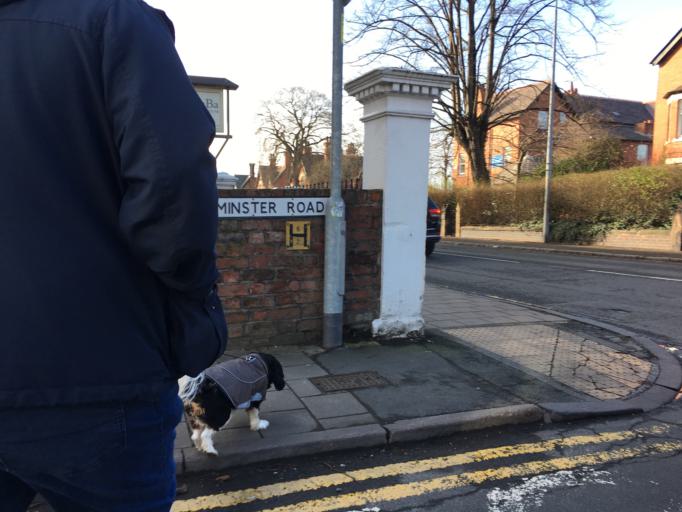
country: GB
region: England
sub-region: Cheshire West and Chester
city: Hoole
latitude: 53.2005
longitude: -2.8757
